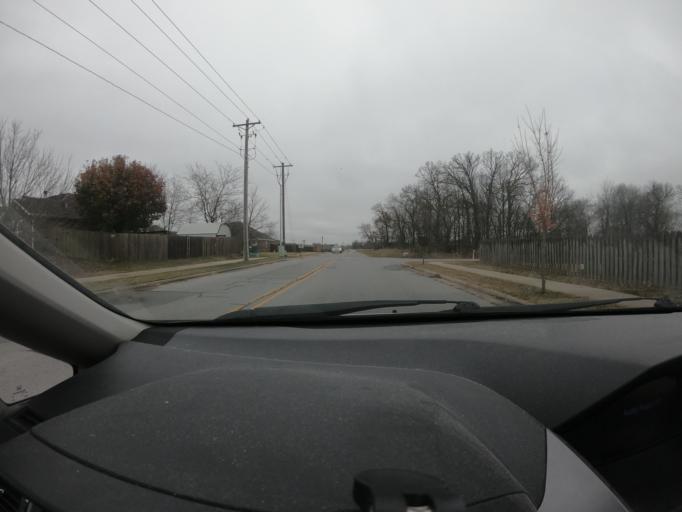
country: US
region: Arkansas
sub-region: Benton County
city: Bentonville
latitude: 36.3511
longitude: -94.2402
